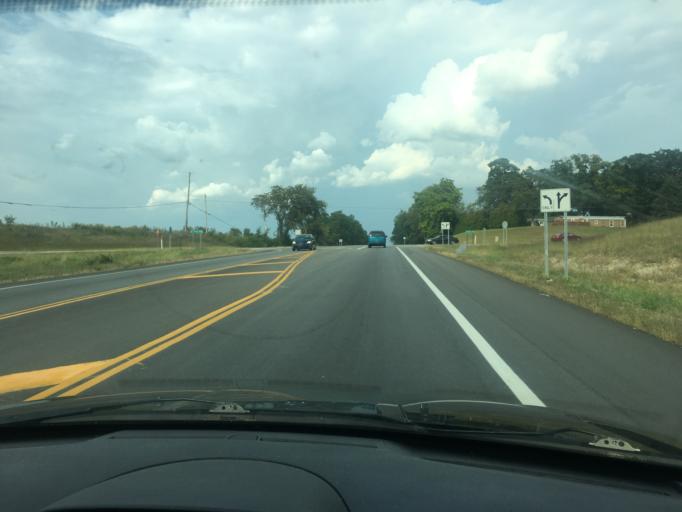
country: US
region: Ohio
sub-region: Champaign County
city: Urbana
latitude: 40.0684
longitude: -83.7731
